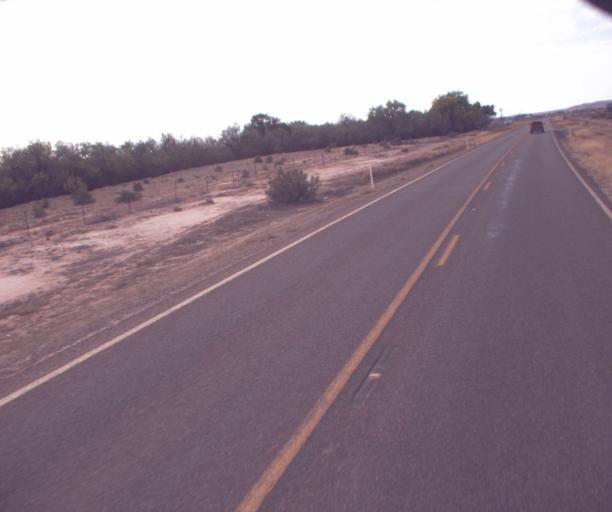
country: US
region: Arizona
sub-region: Apache County
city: Many Farms
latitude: 36.2709
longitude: -109.6002
